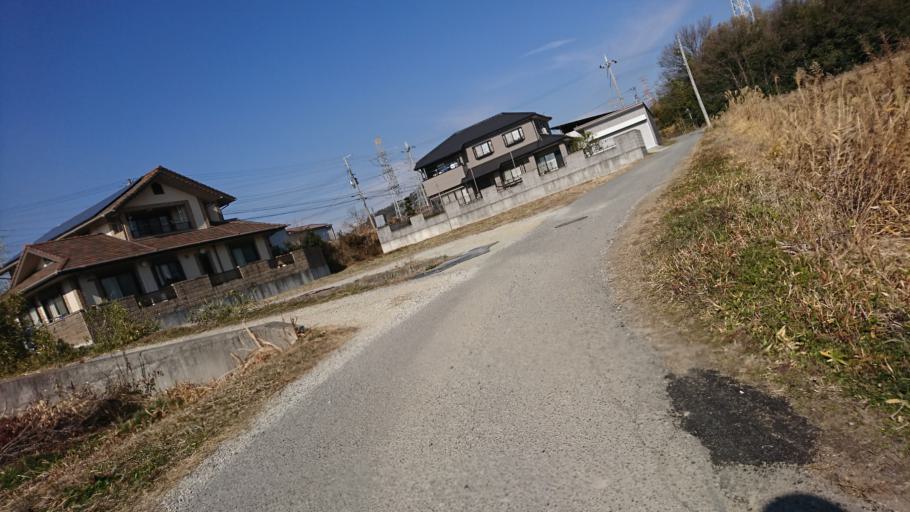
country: JP
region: Hyogo
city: Kakogawacho-honmachi
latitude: 34.8084
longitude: 134.8628
